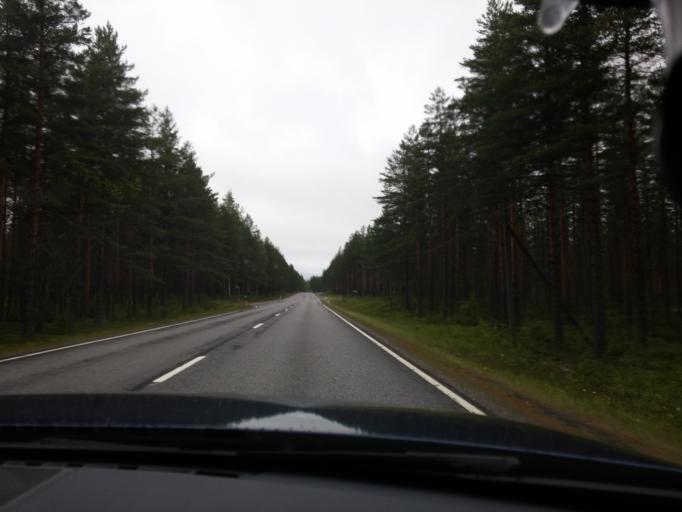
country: FI
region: Pirkanmaa
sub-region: Ylae-Pirkanmaa
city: Vilppula
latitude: 61.9413
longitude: 24.5414
